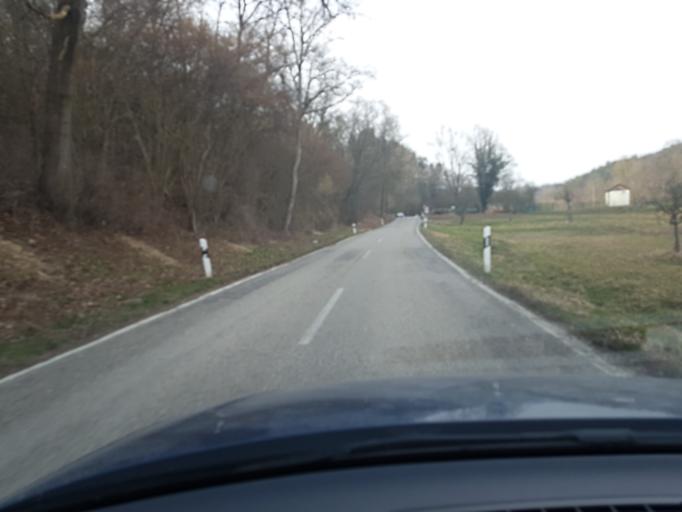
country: DE
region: Baden-Wuerttemberg
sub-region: Regierungsbezirk Stuttgart
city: Eberdingen
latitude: 48.8841
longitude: 8.9622
